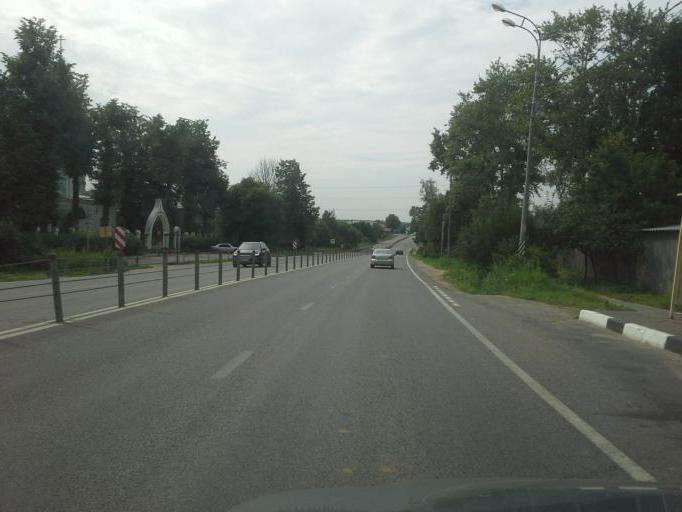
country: RU
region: Moskovskaya
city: Zhavoronki
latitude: 55.6556
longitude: 37.1368
